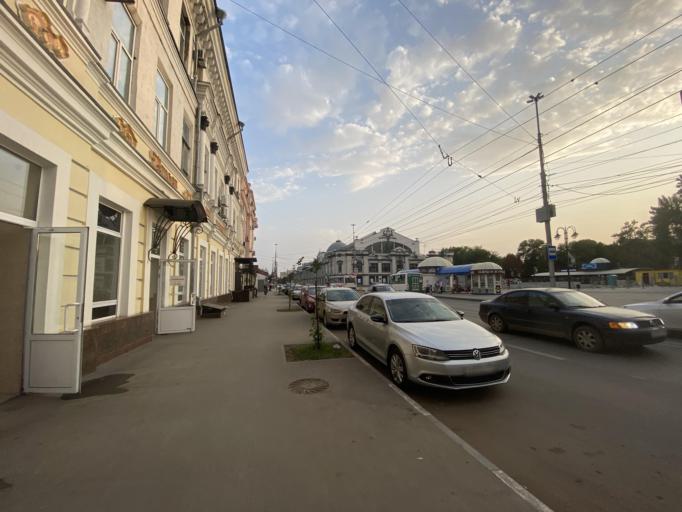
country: RU
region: Saratov
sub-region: Saratovskiy Rayon
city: Saratov
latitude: 51.5336
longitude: 46.0214
